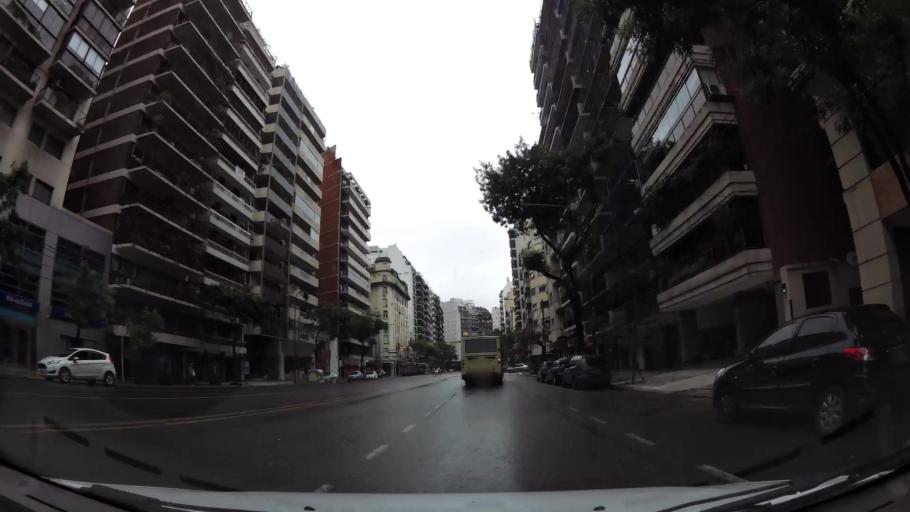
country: AR
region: Buenos Aires F.D.
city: Retiro
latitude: -34.5835
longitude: -58.4051
